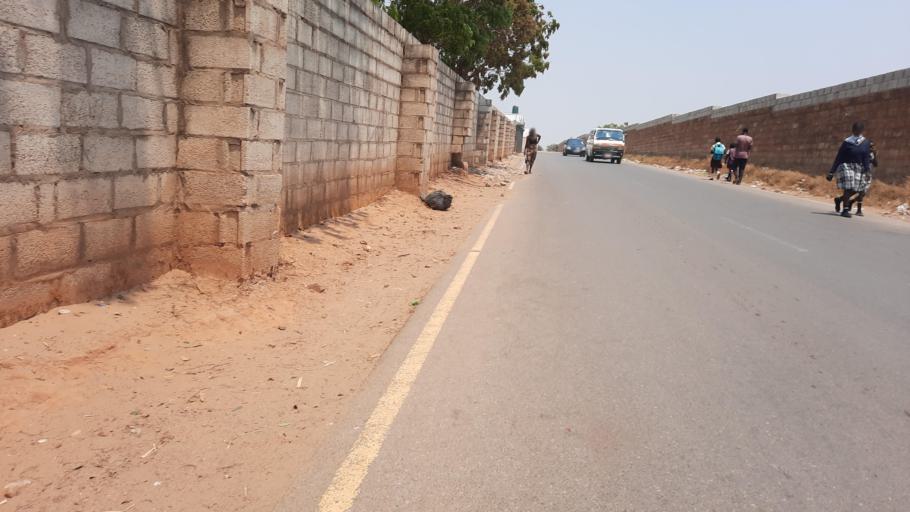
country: ZM
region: Lusaka
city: Lusaka
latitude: -15.4091
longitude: 28.3690
